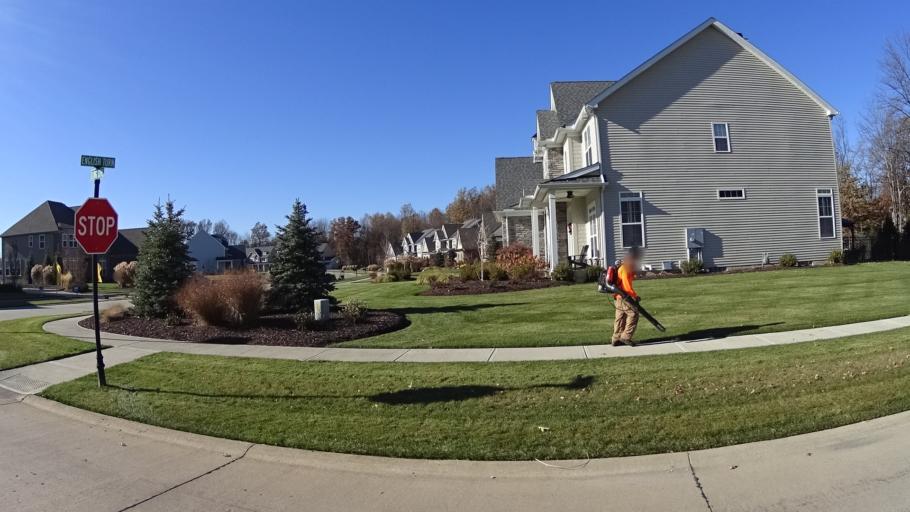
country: US
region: Ohio
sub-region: Lorain County
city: Avon Lake
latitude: 41.4879
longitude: -82.0132
